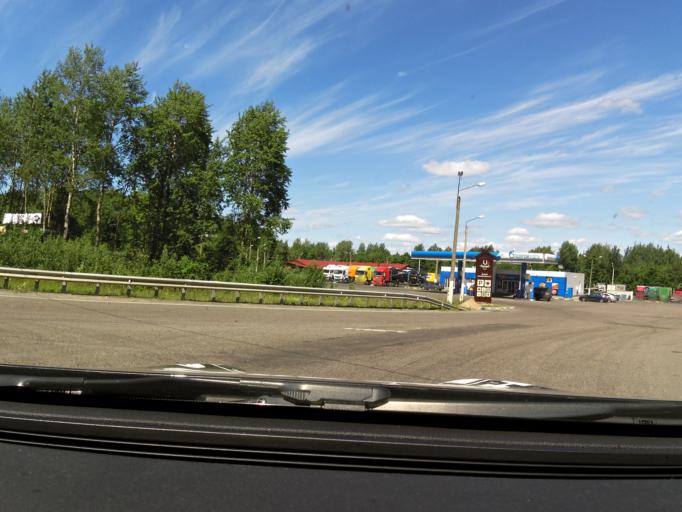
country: RU
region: Novgorod
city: Valday
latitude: 57.9552
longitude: 33.2559
